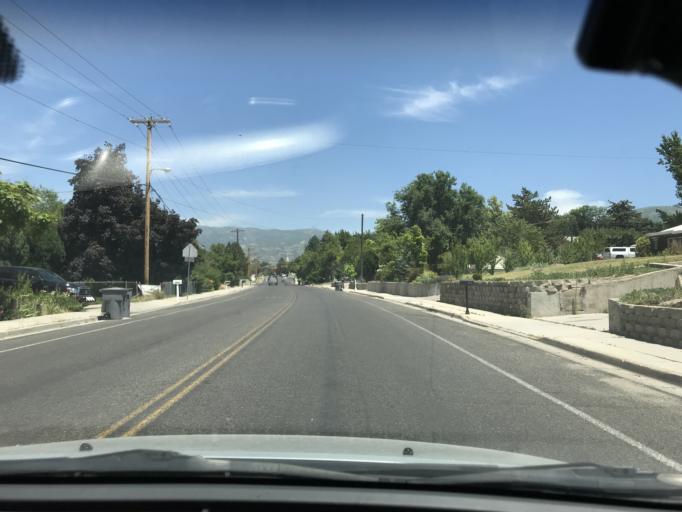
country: US
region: Utah
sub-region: Davis County
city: North Salt Lake
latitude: 40.8470
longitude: -111.8990
